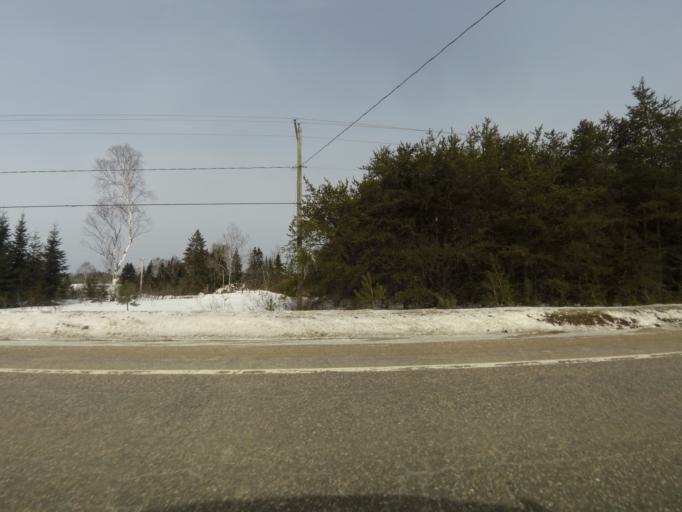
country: CA
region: Quebec
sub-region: Laurentides
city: Ferme-Neuve
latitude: 46.8286
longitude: -75.3181
